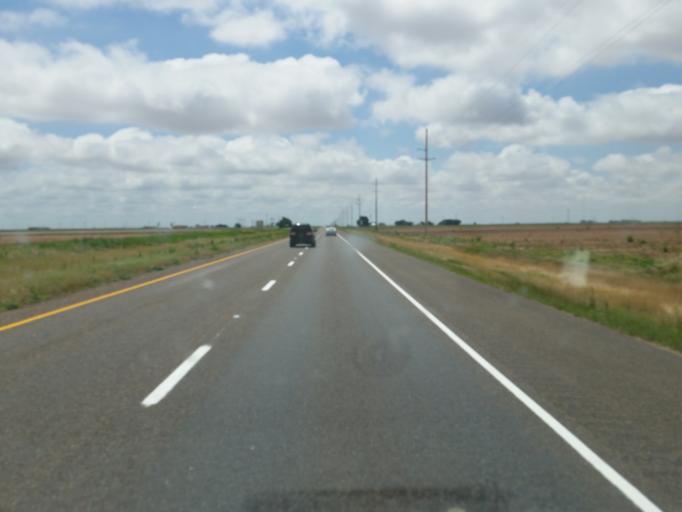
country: US
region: Texas
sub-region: Lubbock County
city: Slaton
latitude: 33.4082
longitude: -101.6243
